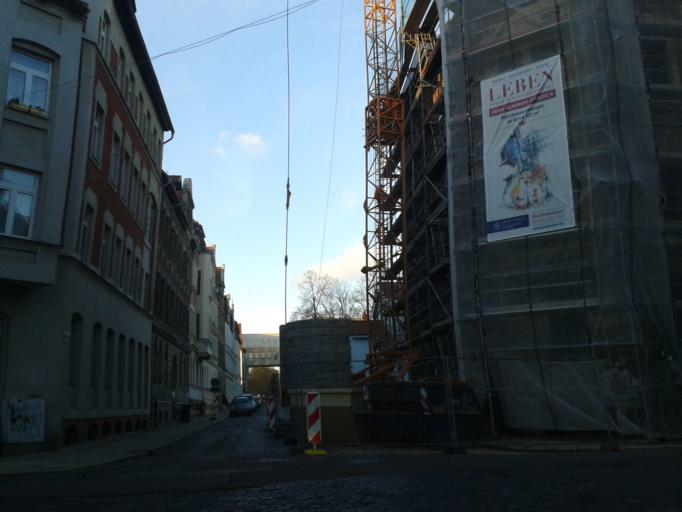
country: DE
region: Saxony-Anhalt
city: Halle (Saale)
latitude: 51.4844
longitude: 11.9618
